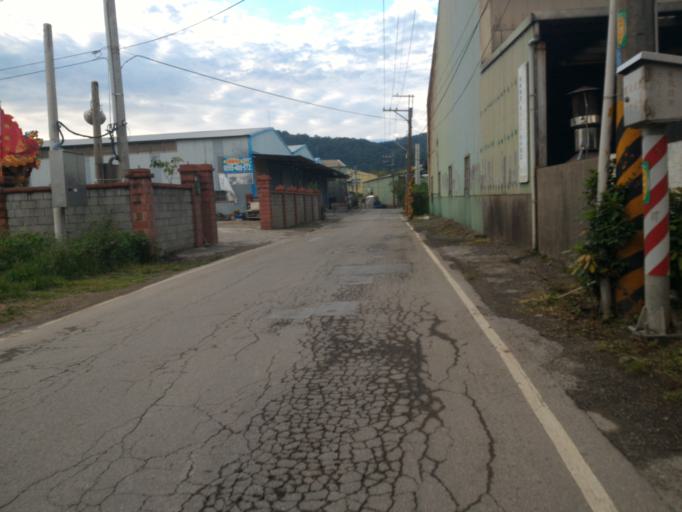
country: TW
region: Taipei
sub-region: Taipei
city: Banqiao
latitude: 24.9530
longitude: 121.4019
